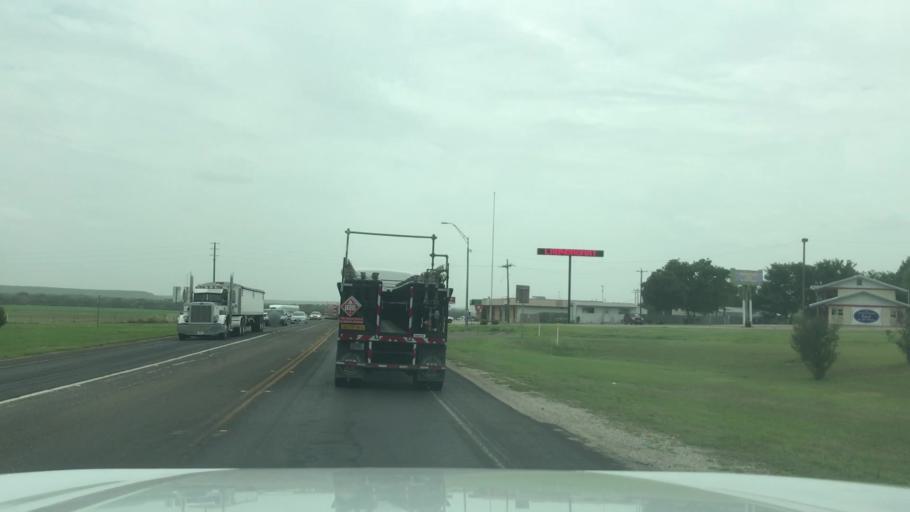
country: US
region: Texas
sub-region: Bosque County
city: Meridian
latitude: 31.9154
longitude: -97.6652
